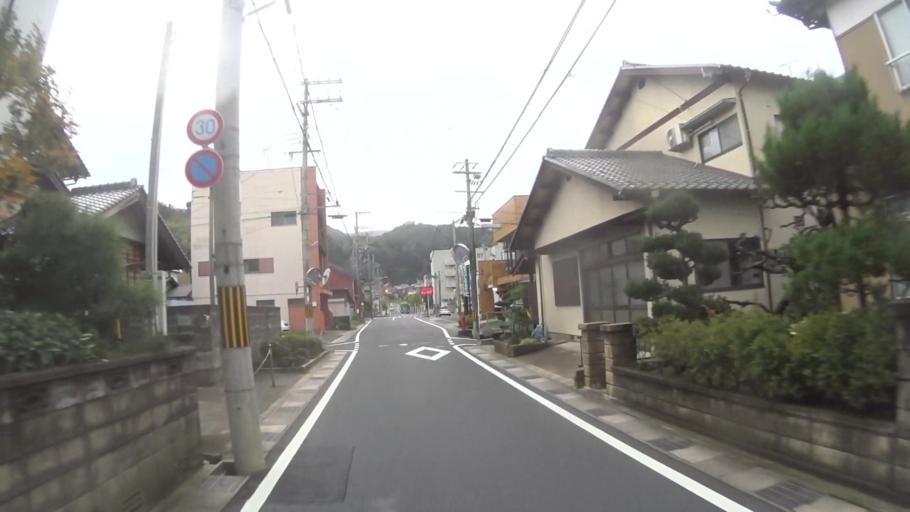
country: JP
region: Kyoto
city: Miyazu
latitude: 35.5340
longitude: 135.2017
